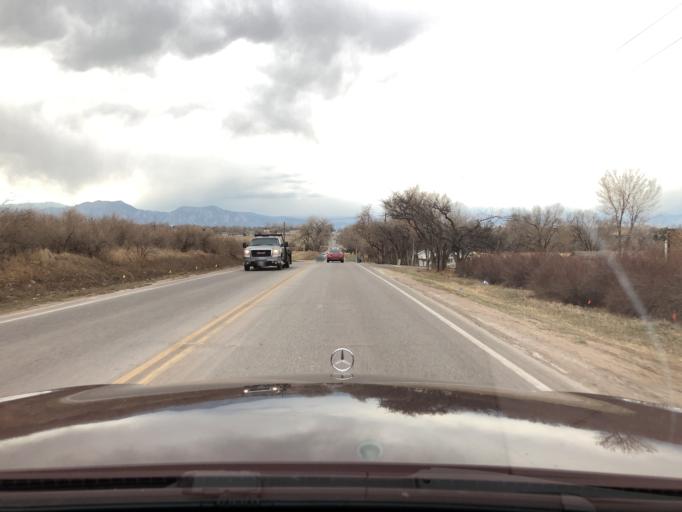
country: US
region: Colorado
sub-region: Boulder County
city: Lafayette
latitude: 40.0148
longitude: -105.1137
